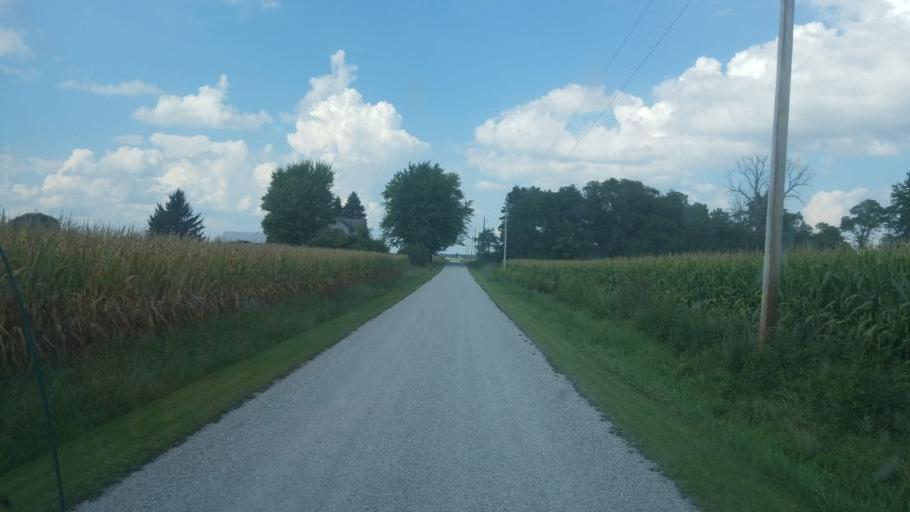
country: US
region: Ohio
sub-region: Huron County
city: Willard
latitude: 40.9921
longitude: -82.7965
